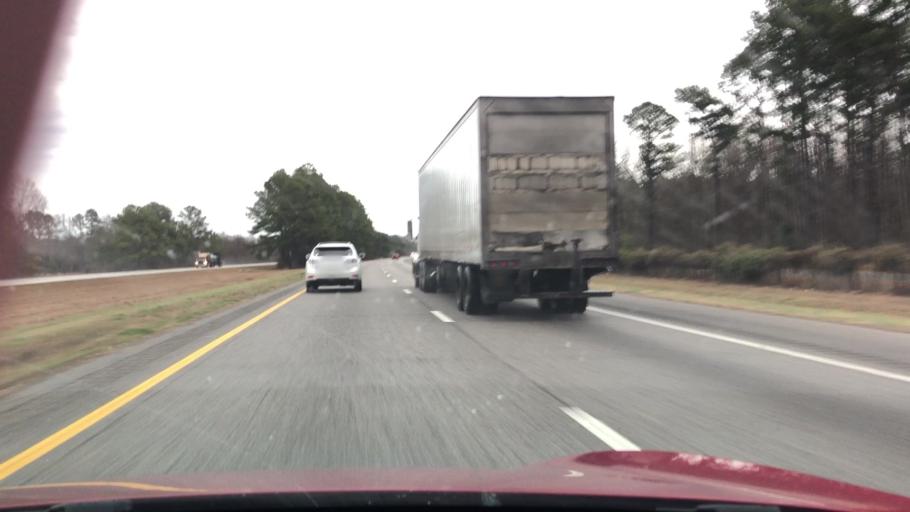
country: US
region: South Carolina
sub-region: Dillon County
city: Latta
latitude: 34.3499
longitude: -79.5242
